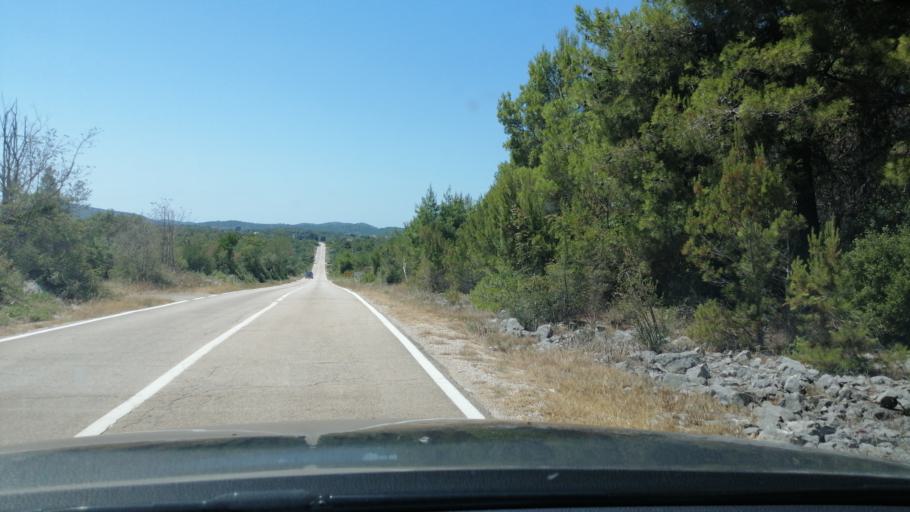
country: HR
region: Sibensko-Kniniska
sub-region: Grad Sibenik
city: Pirovac
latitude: 43.8370
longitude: 15.6889
